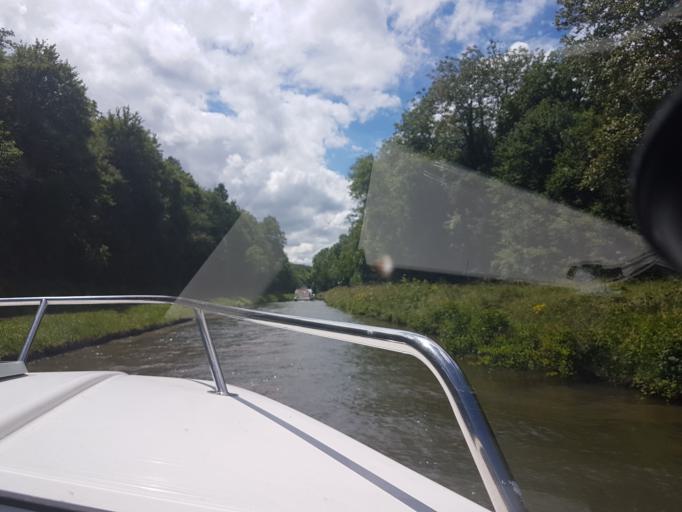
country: FR
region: Bourgogne
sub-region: Departement de l'Yonne
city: Vermenton
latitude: 47.5904
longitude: 3.6598
